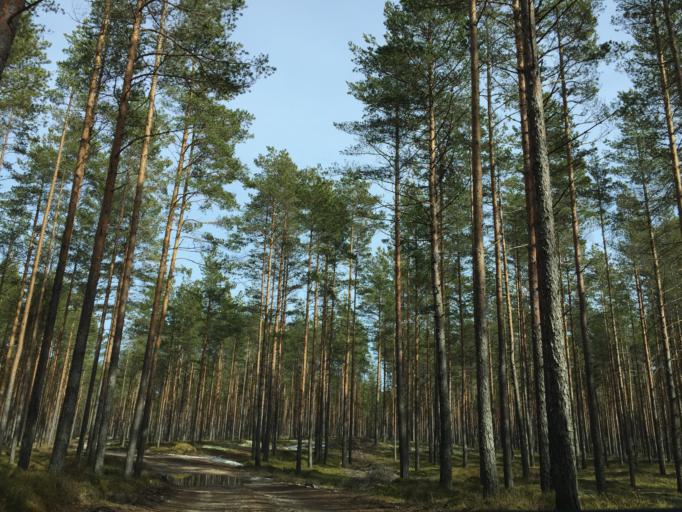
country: EE
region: Paernumaa
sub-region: Paernu linn
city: Parnu
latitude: 58.2413
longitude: 24.5283
